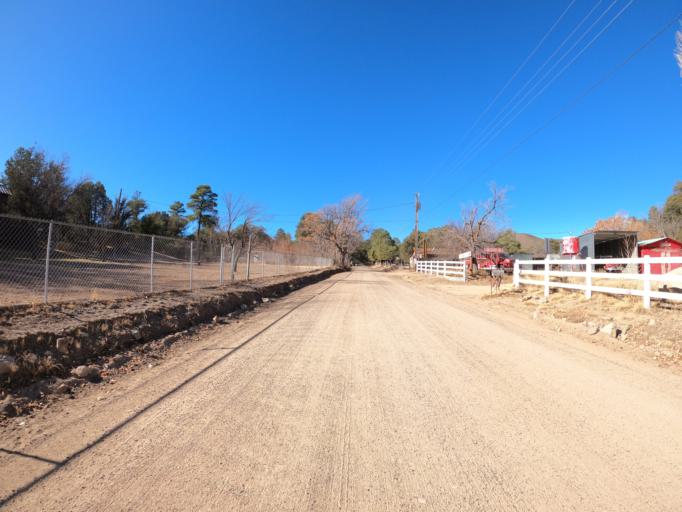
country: US
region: Arizona
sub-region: Yavapai County
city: Verde Village
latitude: 34.5877
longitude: -112.0475
